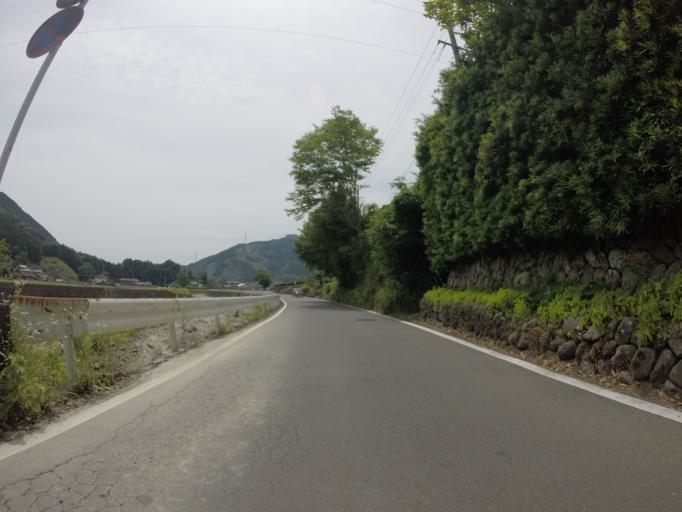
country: JP
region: Shizuoka
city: Shizuoka-shi
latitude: 35.0159
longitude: 138.2806
